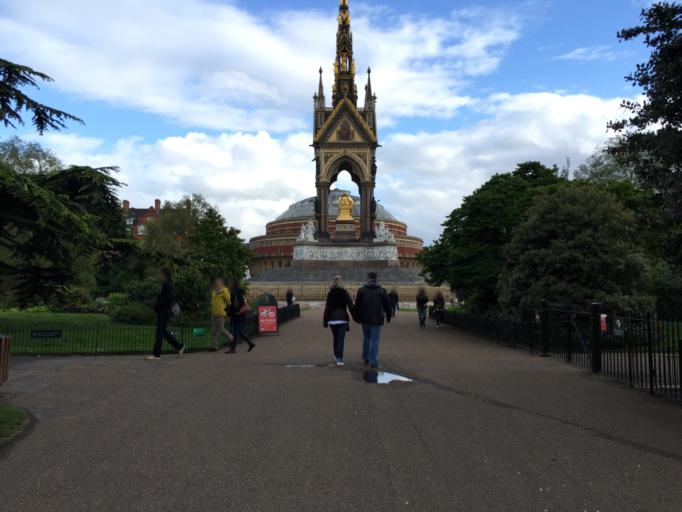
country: GB
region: England
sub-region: Greater London
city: Bayswater
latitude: 51.5032
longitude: -0.1778
